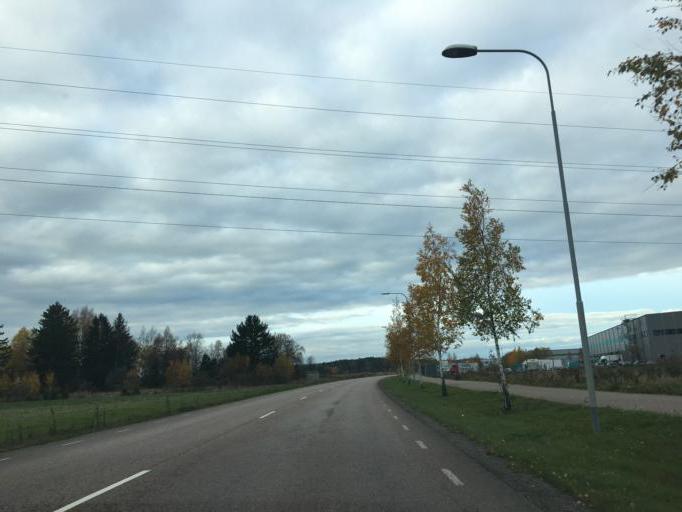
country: SE
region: Vaestmanland
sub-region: Vasteras
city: Vasteras
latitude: 59.5842
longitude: 16.4620
